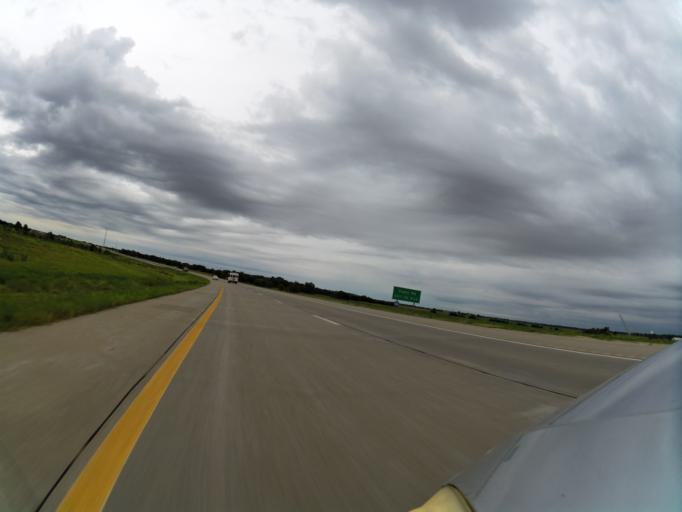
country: US
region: Kansas
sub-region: Reno County
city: Haven
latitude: 37.9385
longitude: -97.8789
